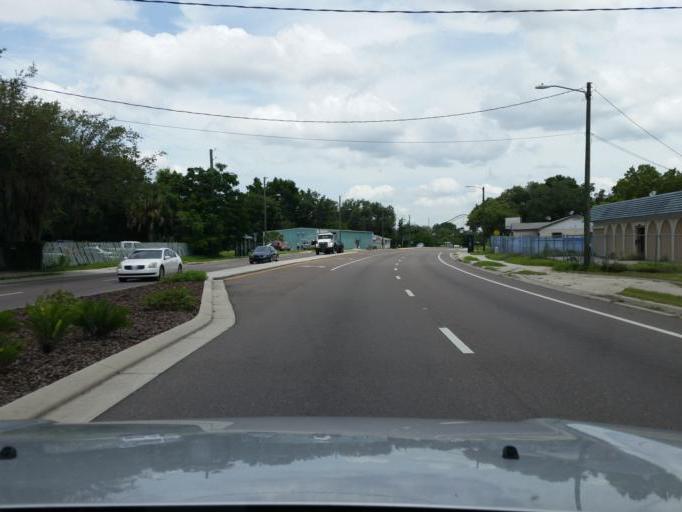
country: US
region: Florida
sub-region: Hillsborough County
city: Temple Terrace
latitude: 28.0242
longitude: -82.4161
